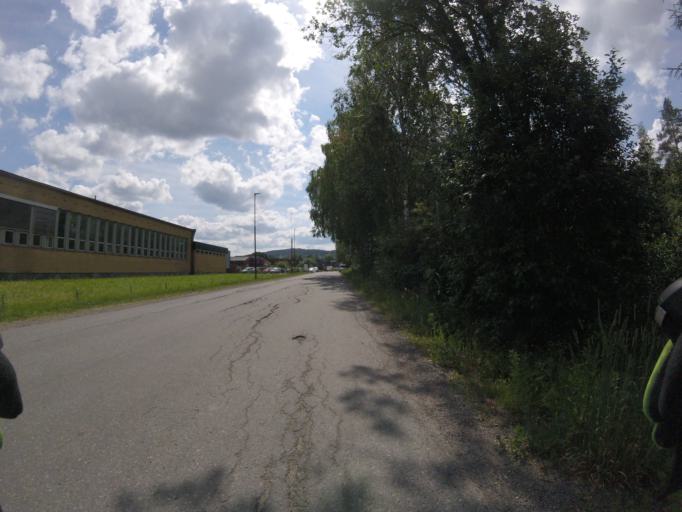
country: NO
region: Akershus
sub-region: Skedsmo
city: Lillestrom
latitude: 59.9606
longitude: 11.0207
